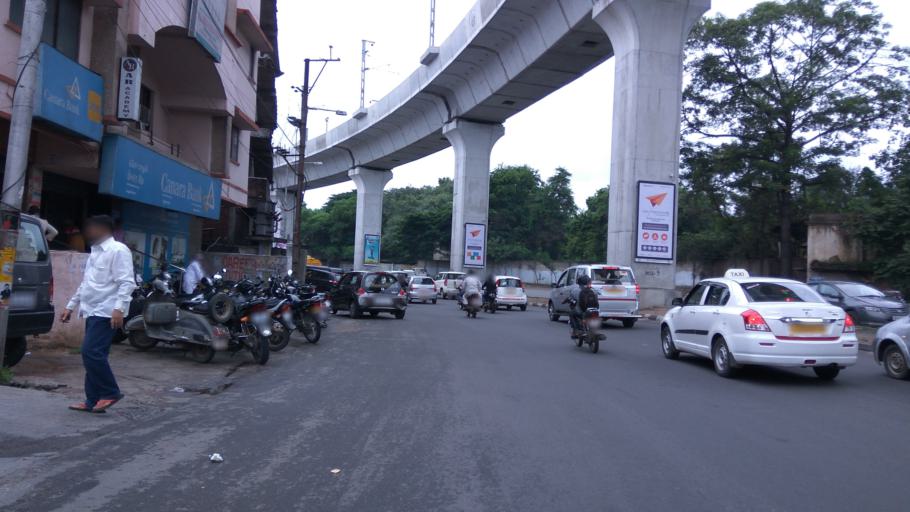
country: IN
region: Telangana
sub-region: Hyderabad
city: Malkajgiri
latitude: 17.4369
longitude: 78.5177
